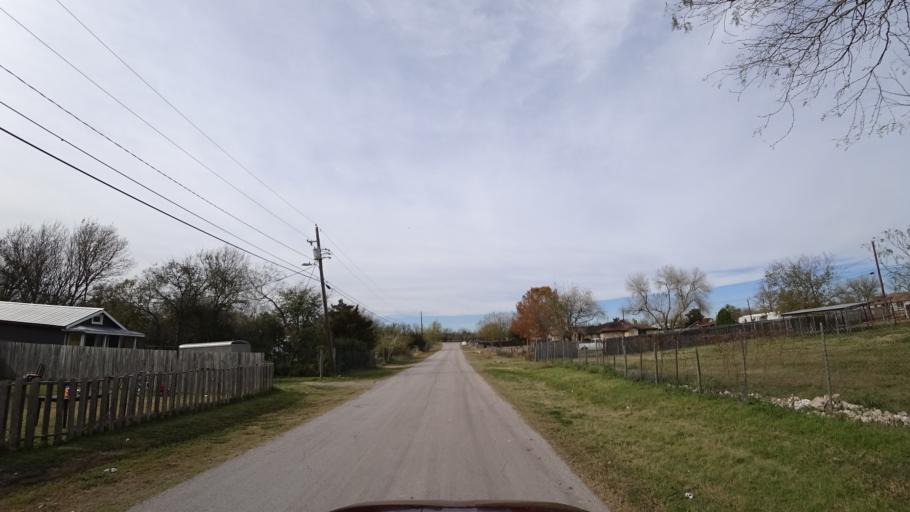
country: US
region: Texas
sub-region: Travis County
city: Garfield
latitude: 30.1298
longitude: -97.6221
